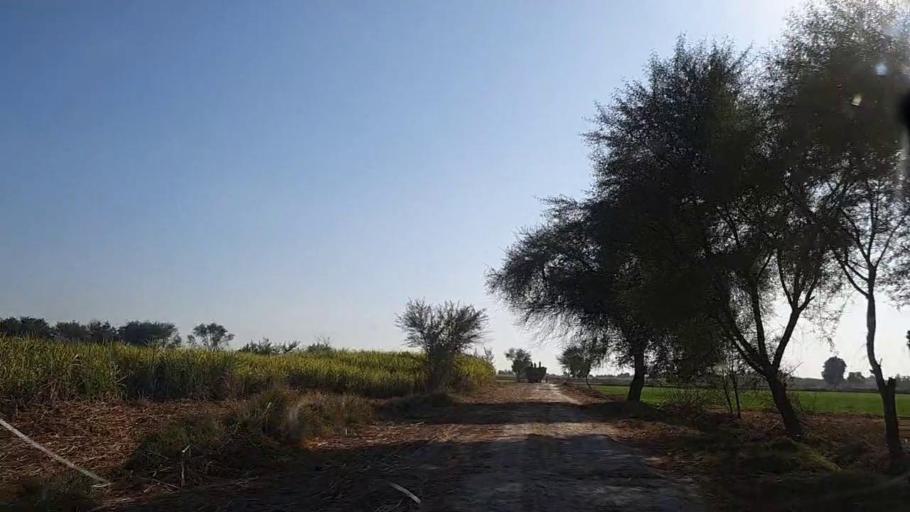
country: PK
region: Sindh
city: Khanpur
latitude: 27.7777
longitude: 69.3661
